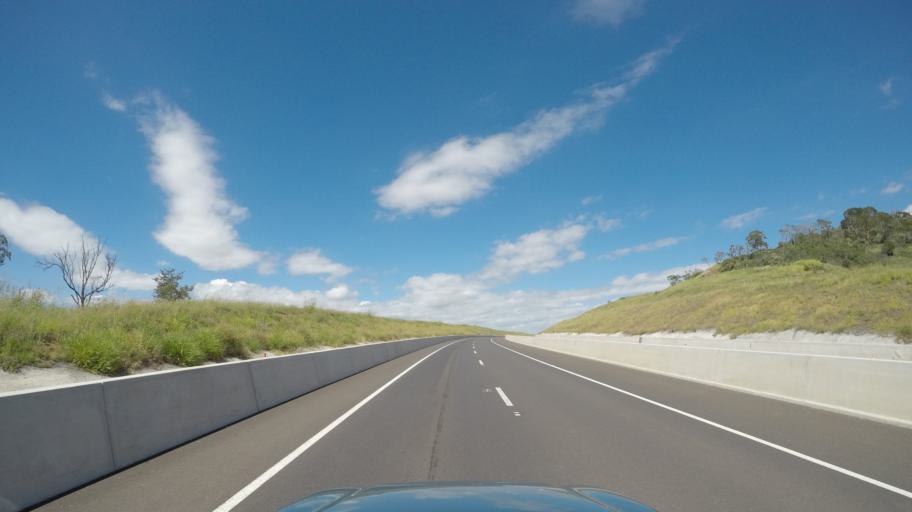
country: AU
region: Queensland
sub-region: Toowoomba
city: Wilsonton Heights
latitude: -27.5110
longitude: 151.8982
